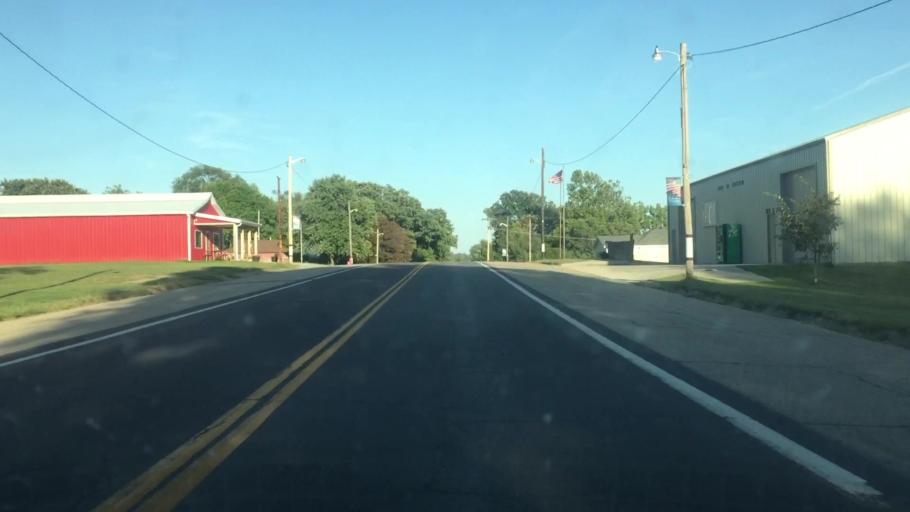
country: US
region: Kansas
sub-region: Brown County
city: Horton
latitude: 39.5505
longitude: -95.5212
